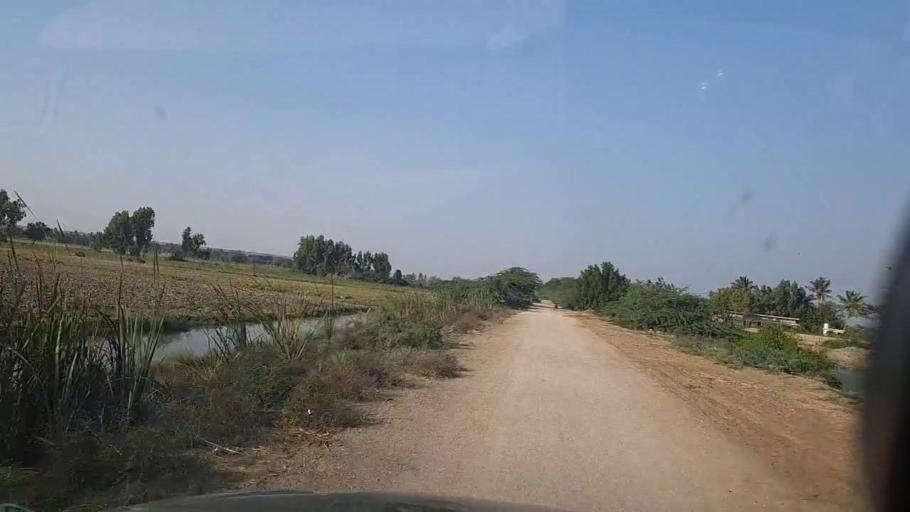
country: PK
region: Sindh
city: Thatta
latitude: 24.6165
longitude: 67.8762
